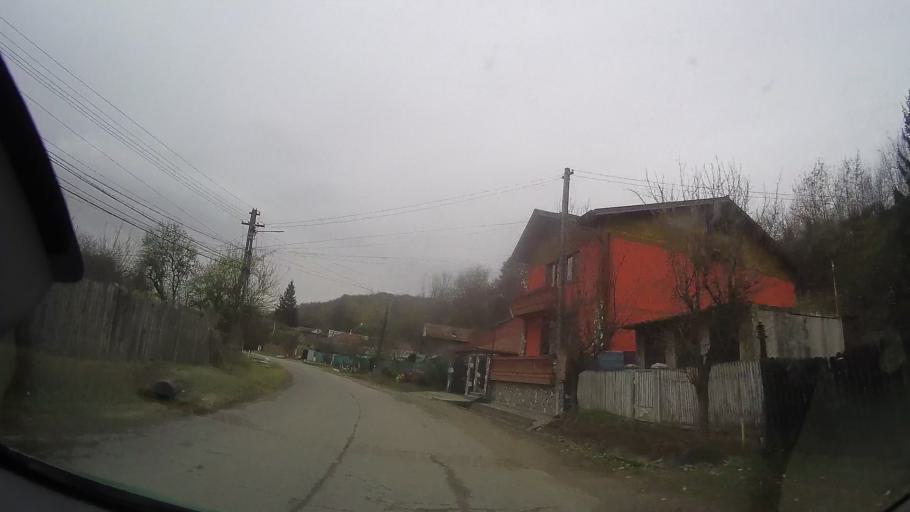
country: RO
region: Prahova
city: Ceptura de Sus
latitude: 45.0373
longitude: 26.3125
